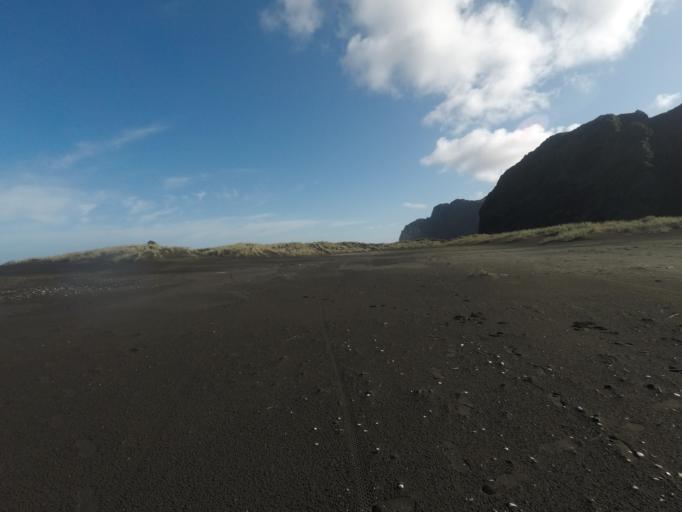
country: NZ
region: Auckland
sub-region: Auckland
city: Muriwai Beach
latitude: -36.9964
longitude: 174.4743
